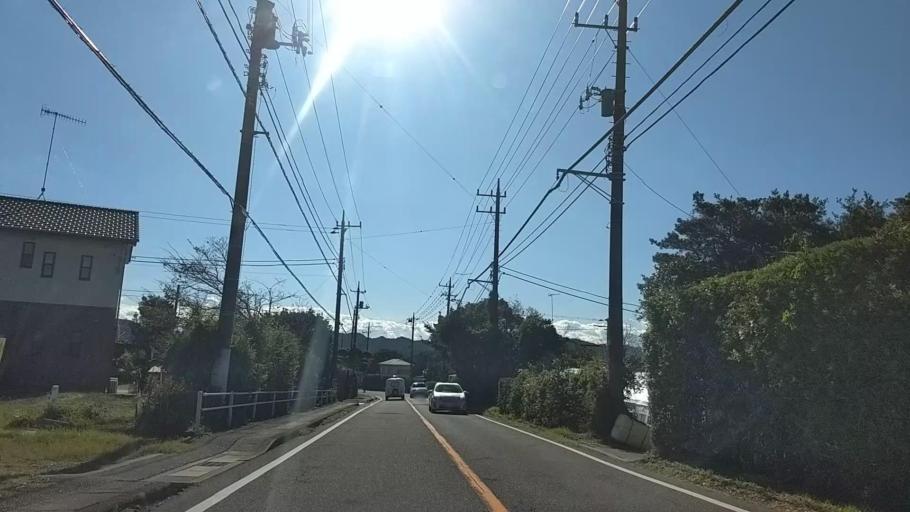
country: JP
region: Chiba
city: Tateyama
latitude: 34.9448
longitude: 139.8365
